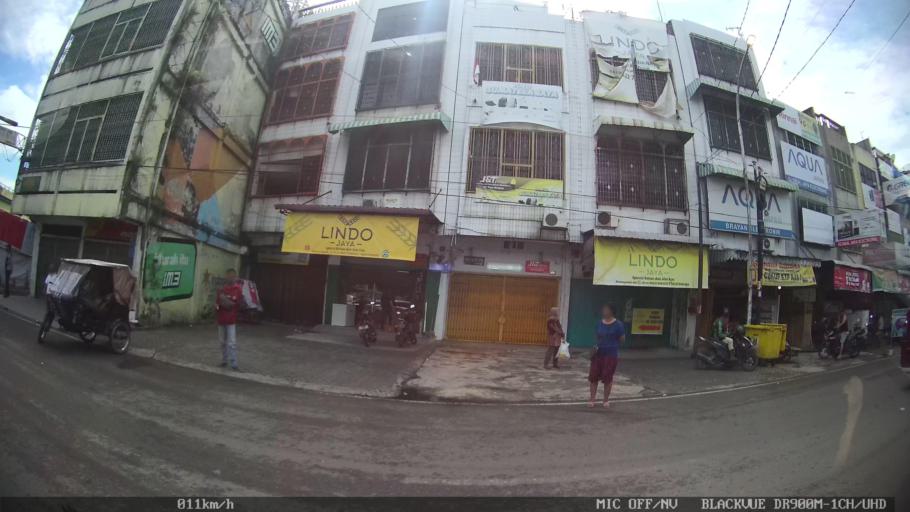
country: ID
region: North Sumatra
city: Medan
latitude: 3.6281
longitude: 98.6695
